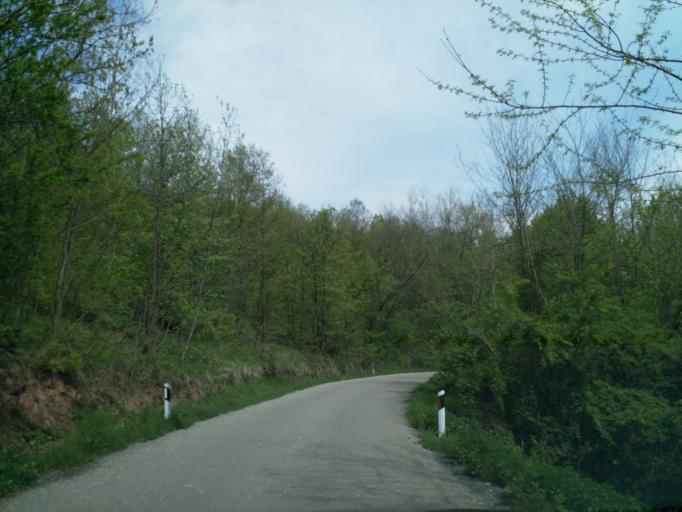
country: RS
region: Central Serbia
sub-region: Pomoravski Okrug
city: Despotovac
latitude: 43.9633
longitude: 21.5588
